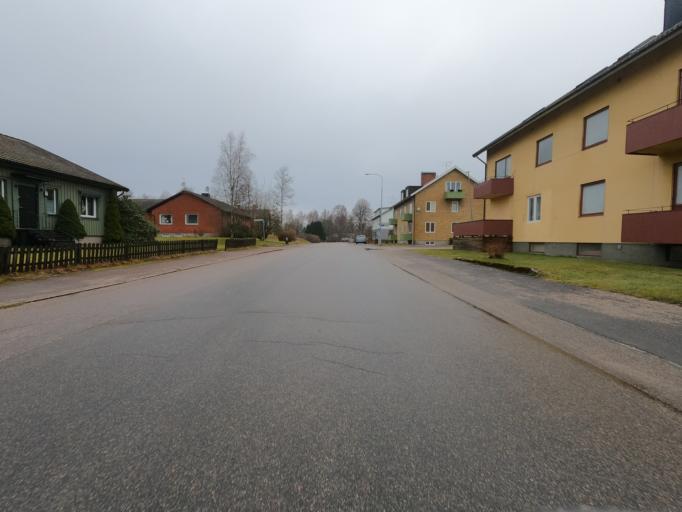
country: SE
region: Halland
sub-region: Hylte Kommun
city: Hyltebruk
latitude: 56.8273
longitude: 13.4457
